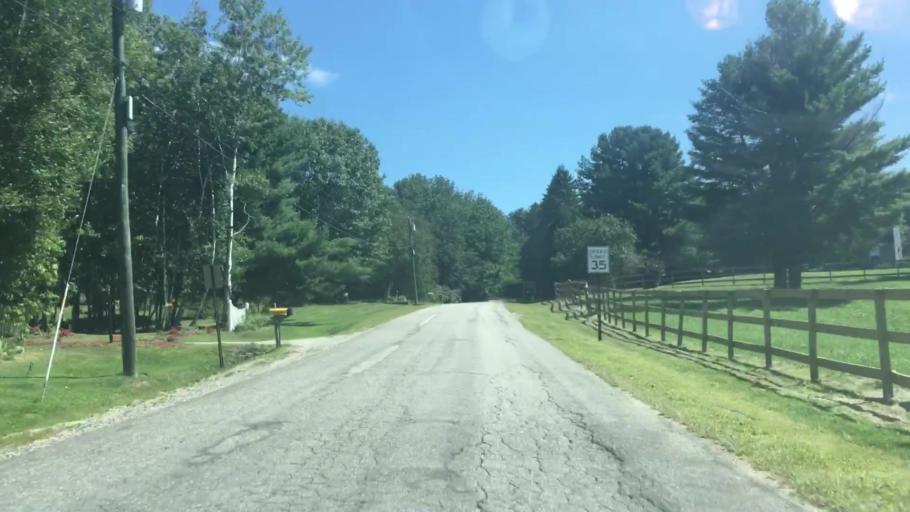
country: US
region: Maine
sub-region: Androscoggin County
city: Sabattus
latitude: 44.1225
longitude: -70.0614
